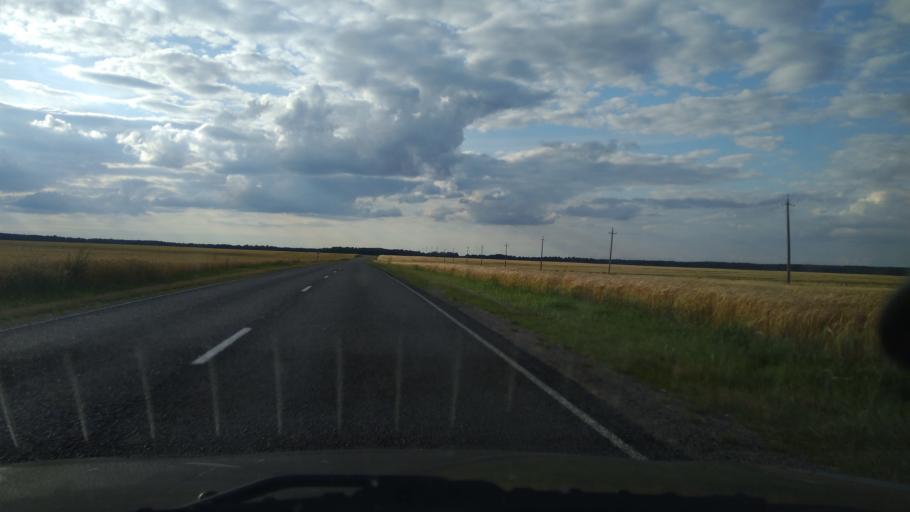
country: BY
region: Grodnenskaya
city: Masty
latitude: 53.3269
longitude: 24.6803
